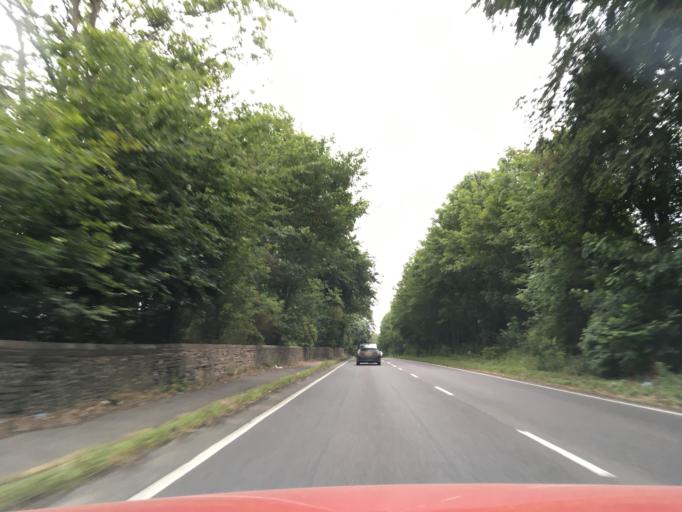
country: GB
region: England
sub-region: Hertfordshire
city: Markyate
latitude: 51.8424
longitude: -0.4673
